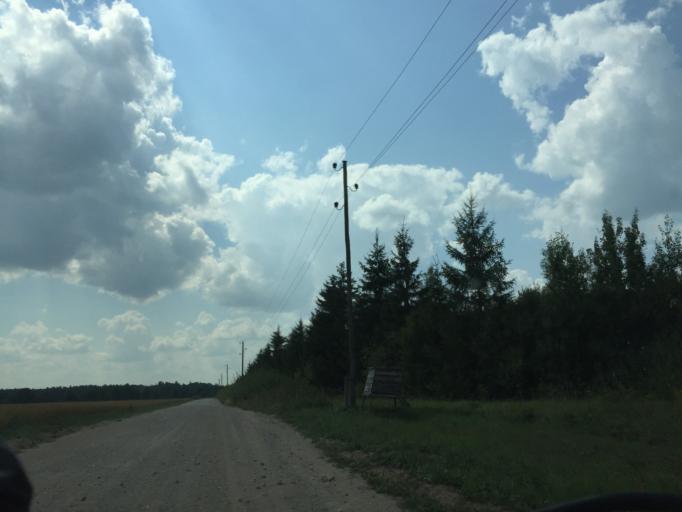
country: LT
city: Zagare
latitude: 56.3826
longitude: 23.1791
